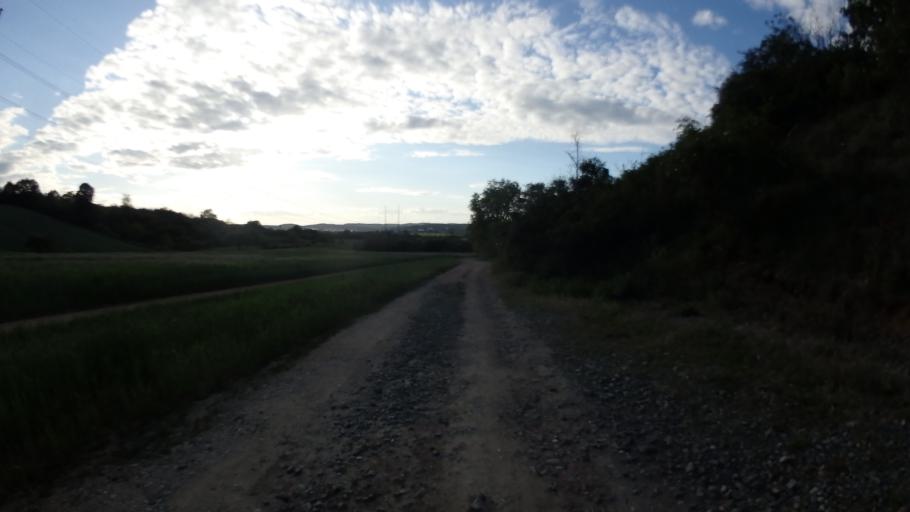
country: CZ
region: South Moravian
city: Ostopovice
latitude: 49.1588
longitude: 16.5398
